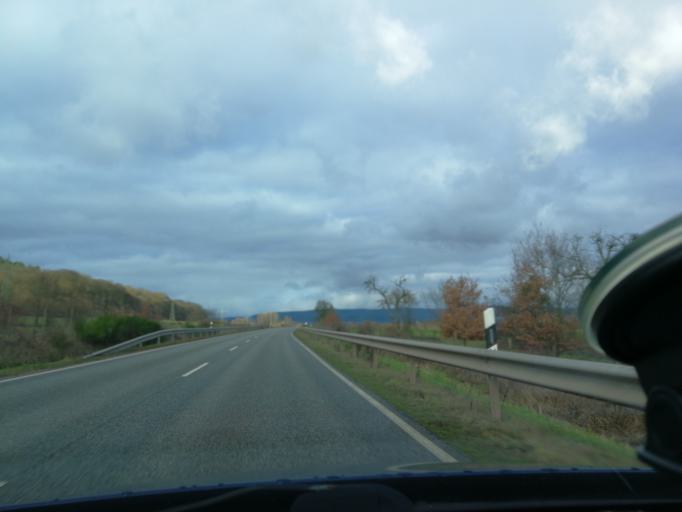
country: DE
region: Rheinland-Pfalz
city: Osann-Monzel
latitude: 49.9320
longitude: 6.9347
